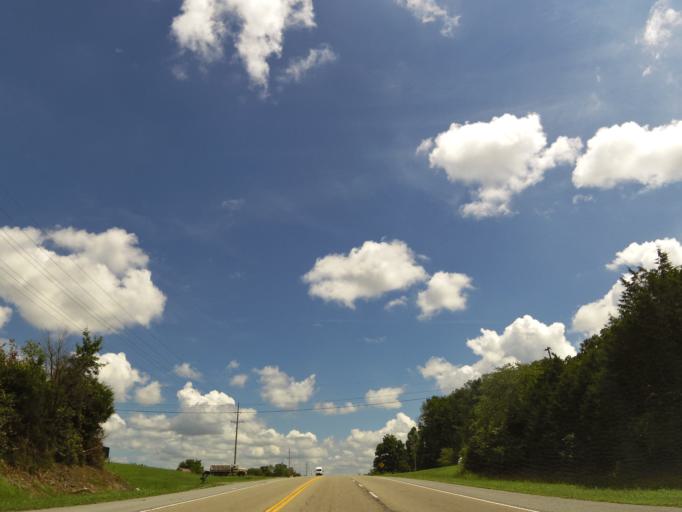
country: US
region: Tennessee
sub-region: Claiborne County
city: Harrogate
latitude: 36.5378
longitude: -83.6879
